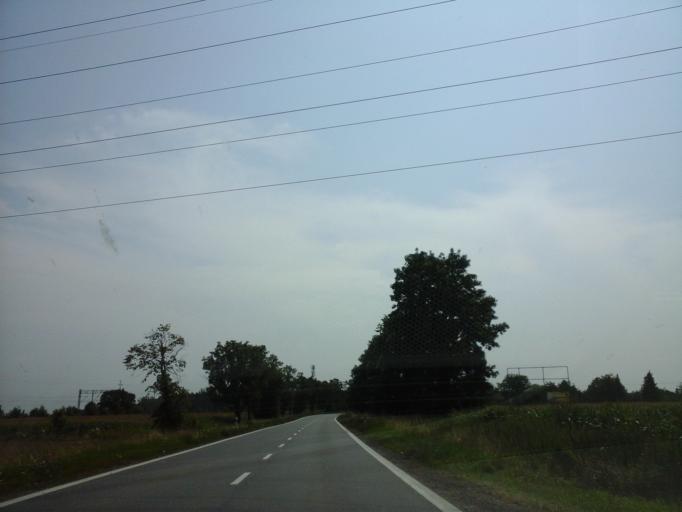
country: PL
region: Lower Silesian Voivodeship
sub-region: Powiat wroclawski
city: Zerniki Wroclawskie
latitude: 51.0364
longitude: 17.0650
